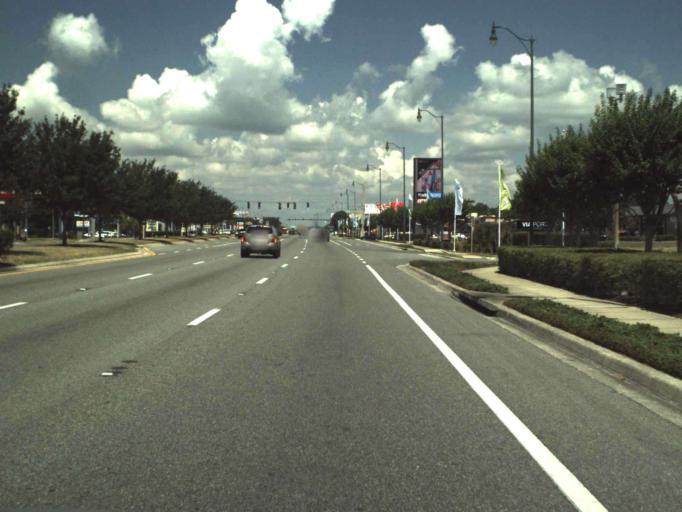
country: US
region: Florida
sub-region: Lake County
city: Silver Lake
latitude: 28.8222
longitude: -81.7831
